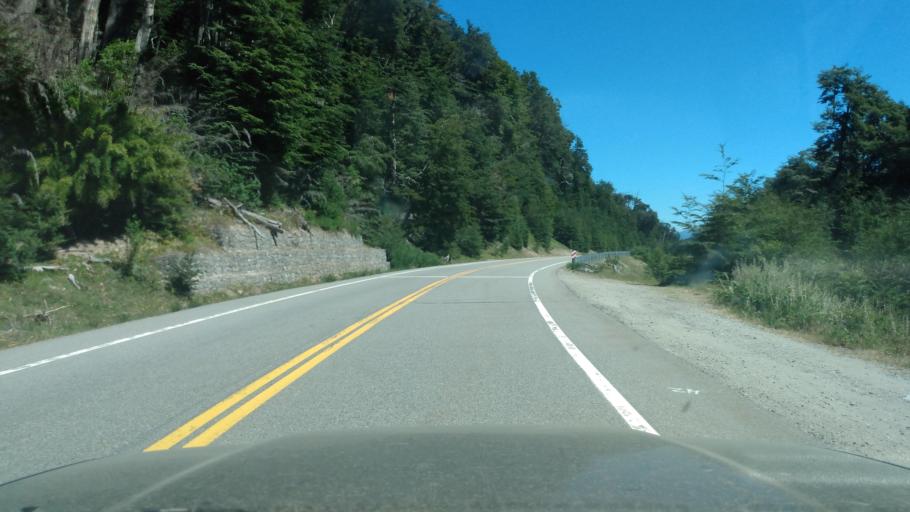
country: AR
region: Neuquen
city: Villa La Angostura
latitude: -40.6106
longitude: -71.6451
